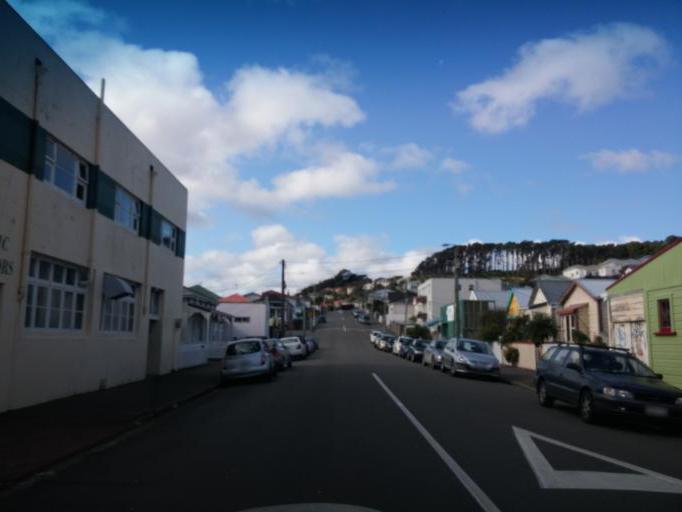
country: NZ
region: Wellington
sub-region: Wellington City
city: Wellington
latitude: -41.3167
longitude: 174.7810
